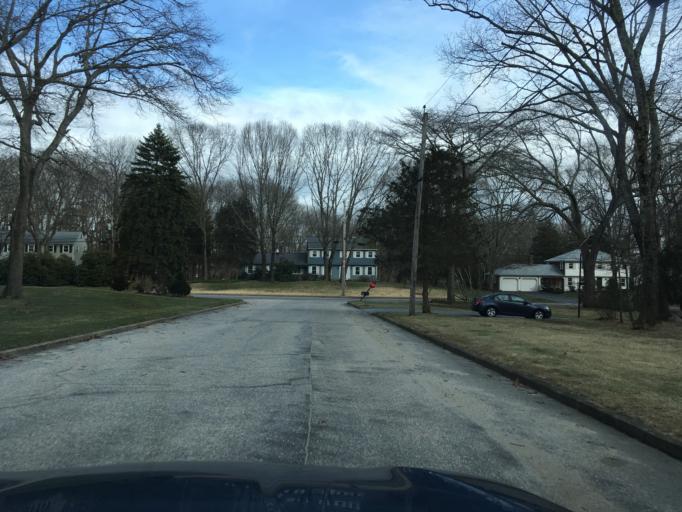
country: US
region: Rhode Island
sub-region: Kent County
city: East Greenwich
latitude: 41.6463
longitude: -71.5008
